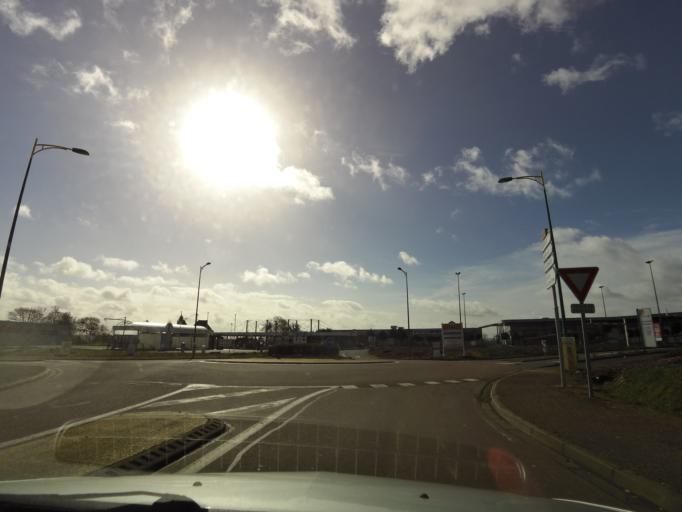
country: FR
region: Lower Normandy
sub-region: Departement de la Manche
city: Agneaux
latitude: 49.1084
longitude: -1.1347
